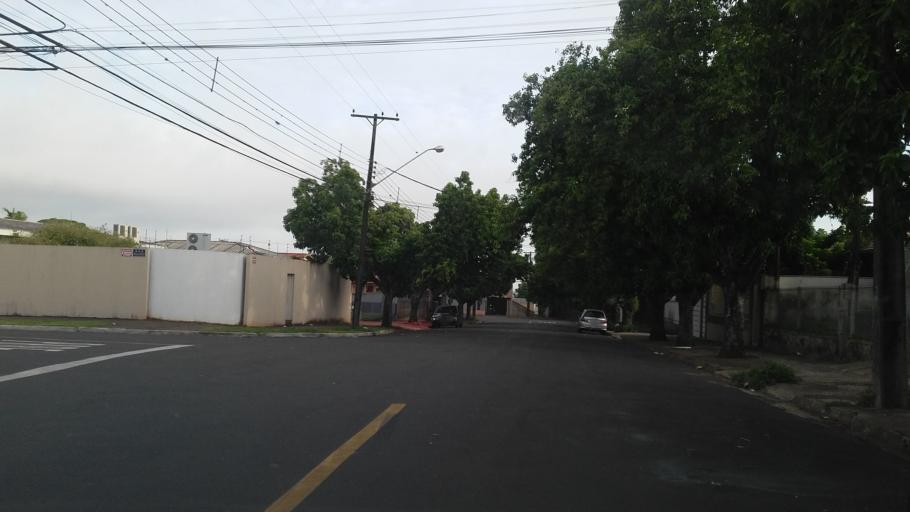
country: BR
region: Parana
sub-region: Londrina
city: Londrina
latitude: -23.3007
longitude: -51.1791
